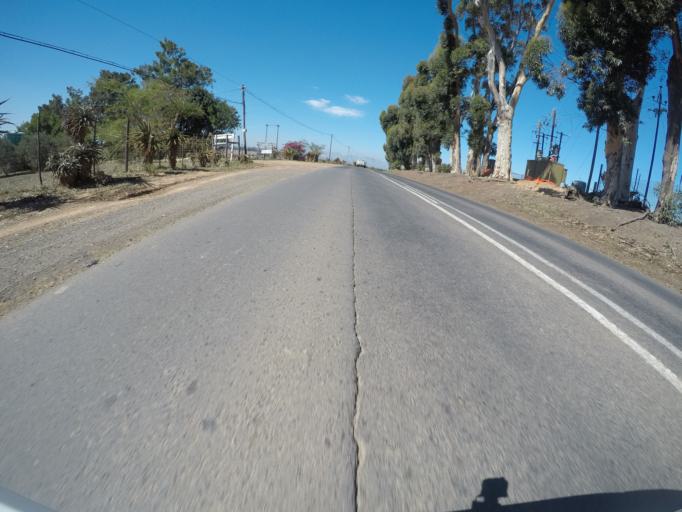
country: ZA
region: Western Cape
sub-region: City of Cape Town
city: Kraaifontein
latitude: -33.8111
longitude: 18.6274
